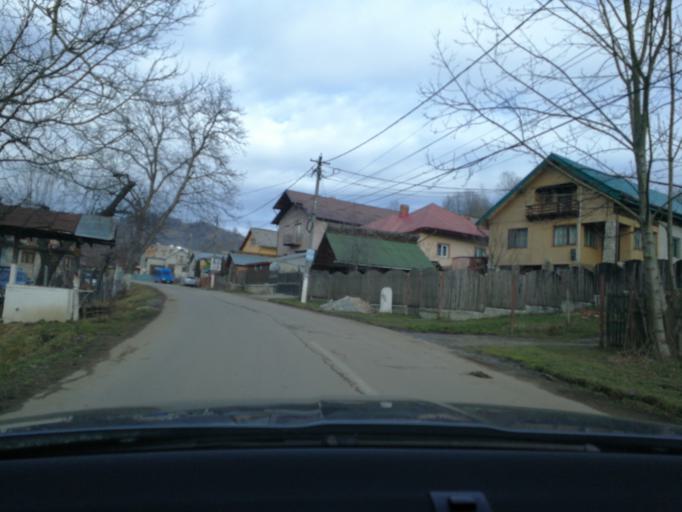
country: RO
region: Prahova
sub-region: Comuna Adunati
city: Ocina de Sus
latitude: 45.1836
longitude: 25.6071
